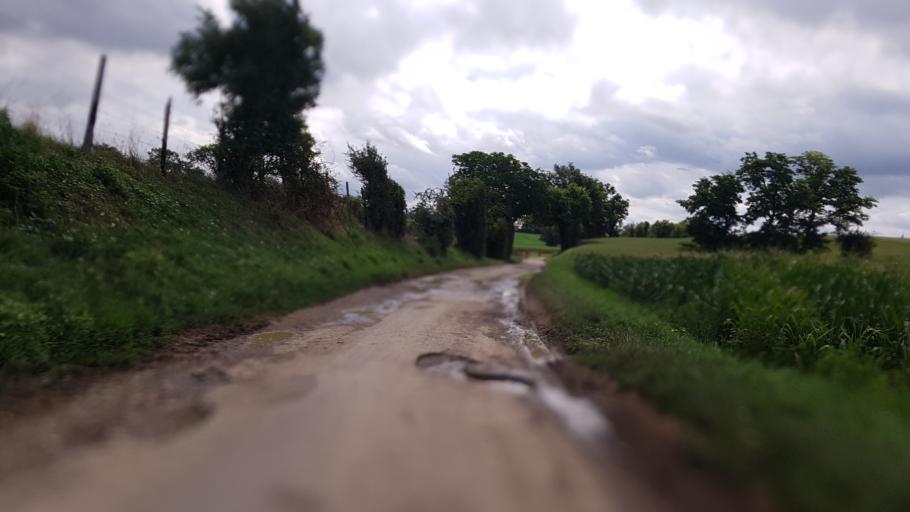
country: FR
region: Rhone-Alpes
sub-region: Departement du Rhone
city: Genas
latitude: 45.7387
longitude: 4.9910
